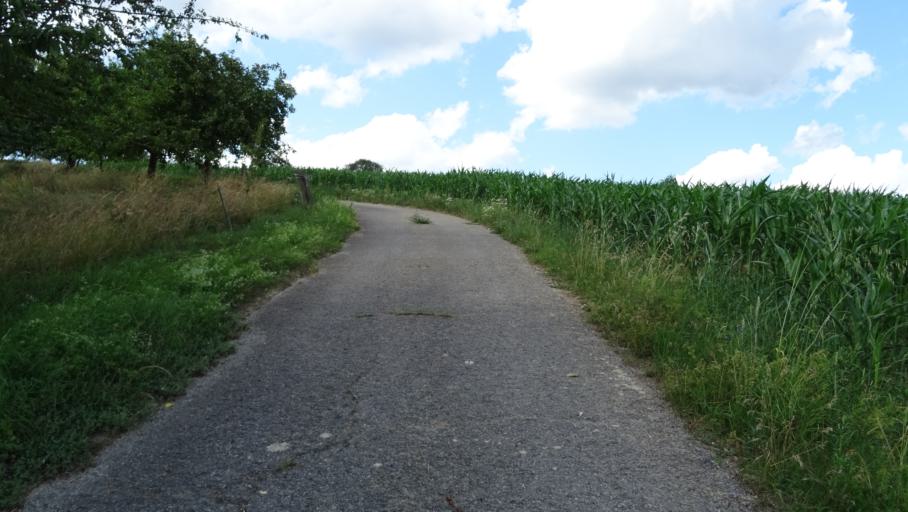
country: DE
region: Baden-Wuerttemberg
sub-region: Karlsruhe Region
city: Limbach
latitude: 49.4270
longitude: 9.2434
